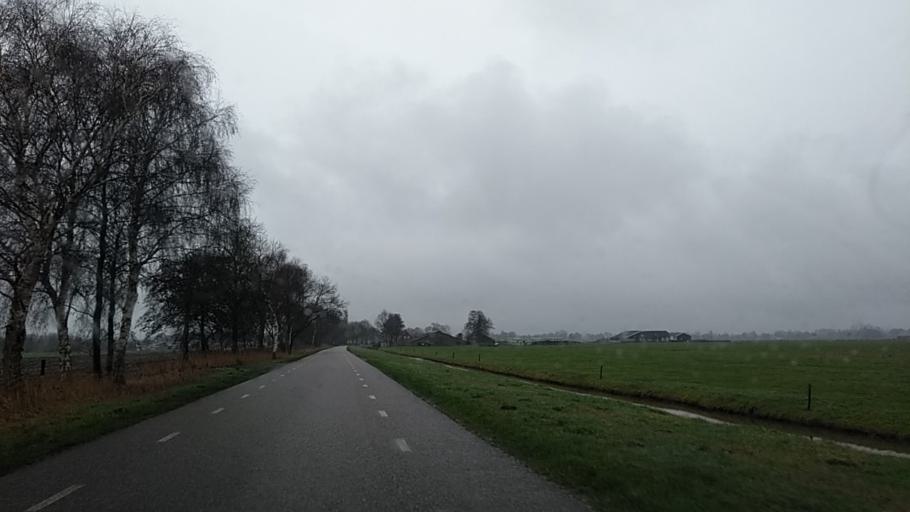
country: NL
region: Overijssel
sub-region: Gemeente Staphorst
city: Staphorst
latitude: 52.6111
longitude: 6.1701
